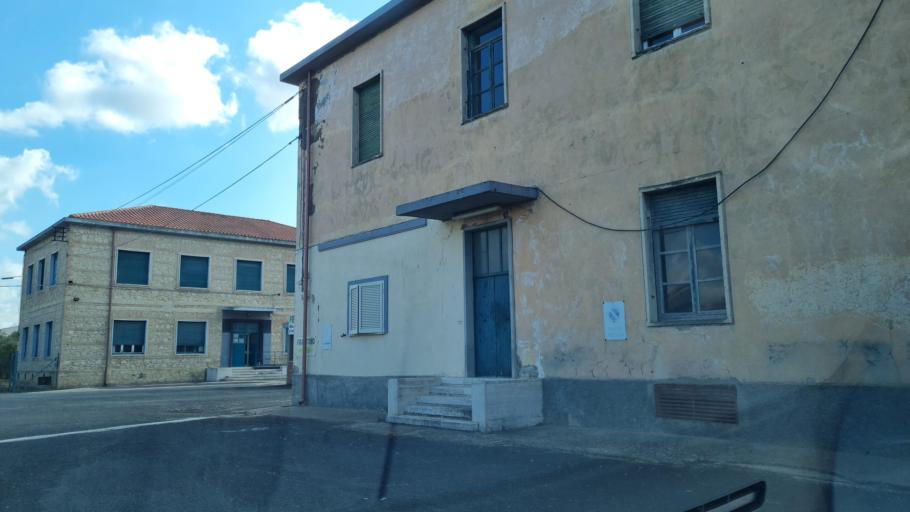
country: IT
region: Latium
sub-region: Provincia di Viterbo
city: Tarquinia
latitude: 42.2604
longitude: 11.7653
